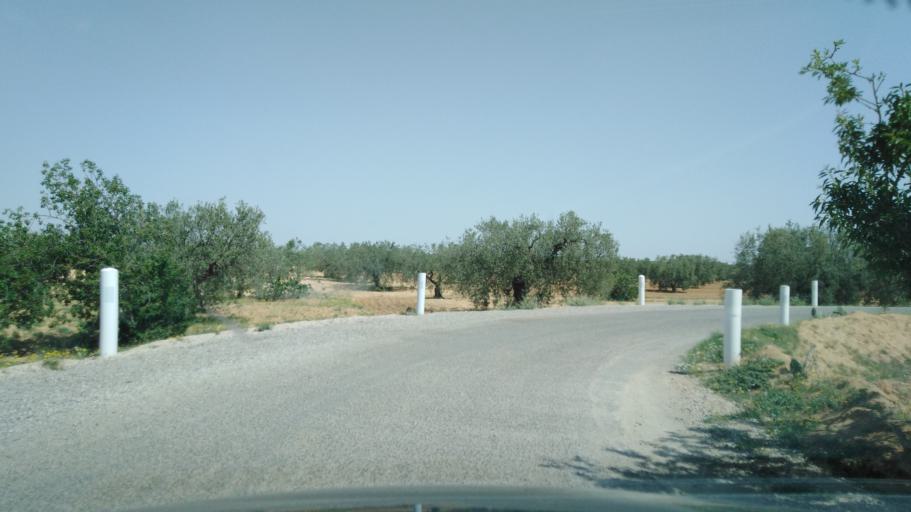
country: TN
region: Safaqis
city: Sfax
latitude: 34.6821
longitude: 10.4372
